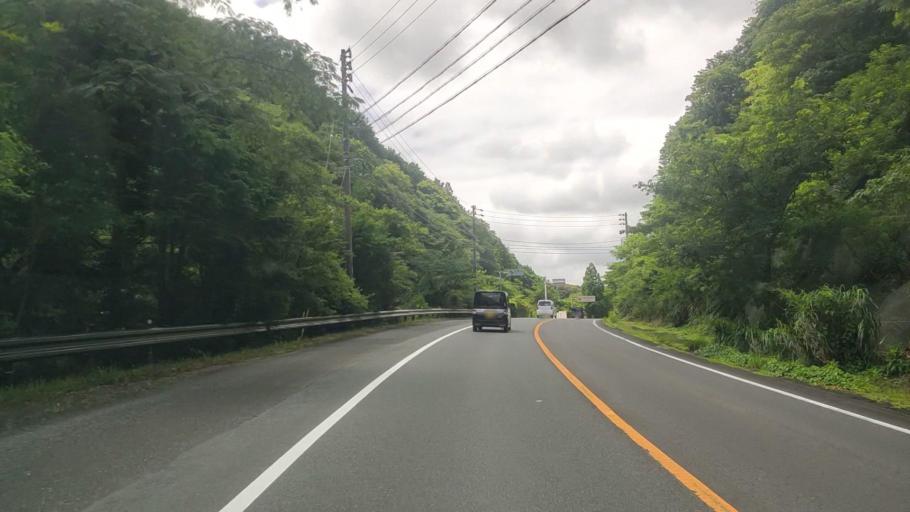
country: JP
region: Mie
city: Toba
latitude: 34.4139
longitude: 136.8160
